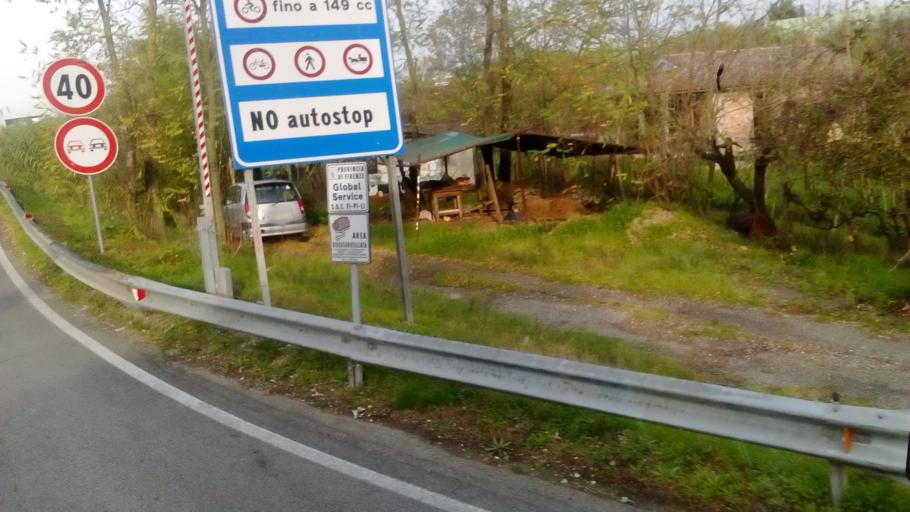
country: IT
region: Tuscany
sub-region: Province of Florence
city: Montelupo Fiorentino
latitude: 43.7210
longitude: 11.0086
